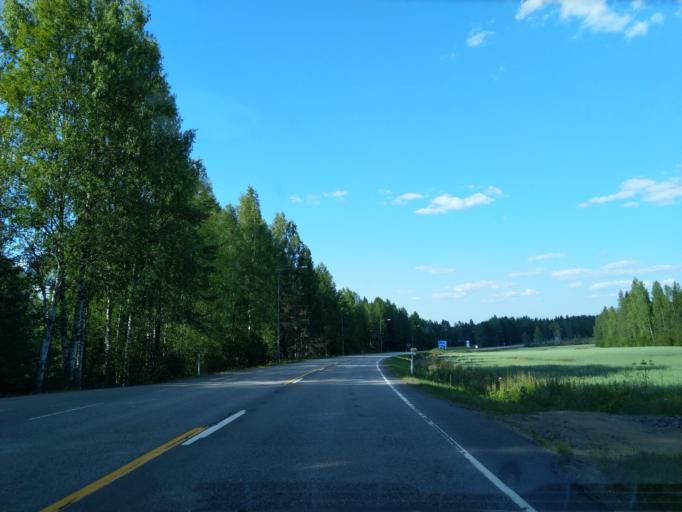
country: FI
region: Pirkanmaa
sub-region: Luoteis-Pirkanmaa
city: Kihnioe
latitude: 62.1940
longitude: 23.1713
